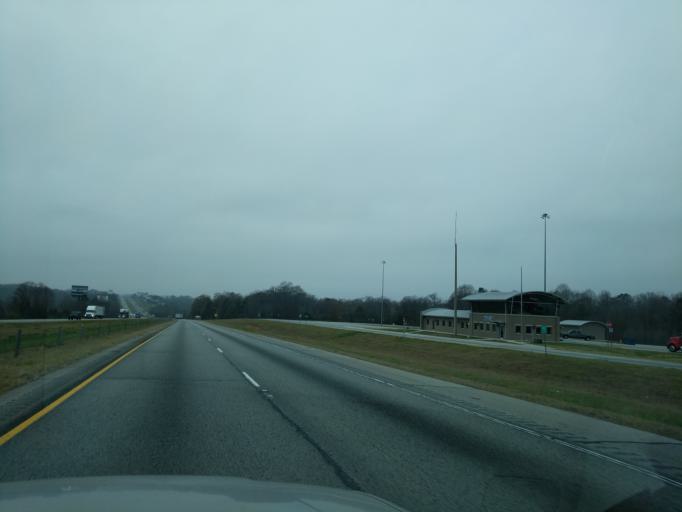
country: US
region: Georgia
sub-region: Franklin County
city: Lavonia
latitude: 34.4161
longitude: -83.1747
